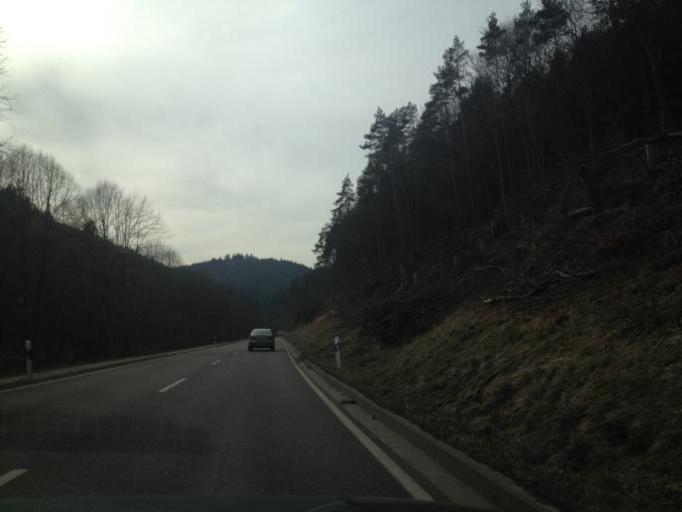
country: DE
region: Rheinland-Pfalz
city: Altleiningen
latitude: 49.4533
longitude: 8.0748
